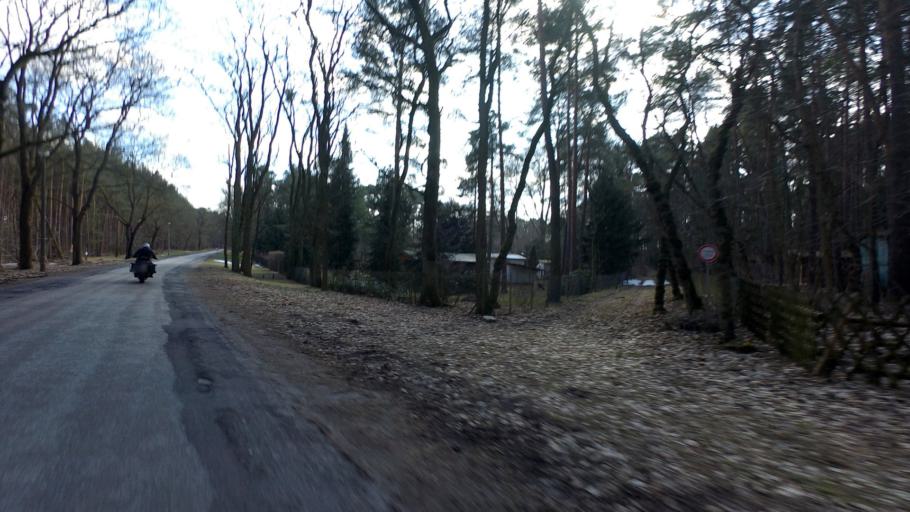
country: DE
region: Brandenburg
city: Biesenthal
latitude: 52.7783
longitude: 13.6146
